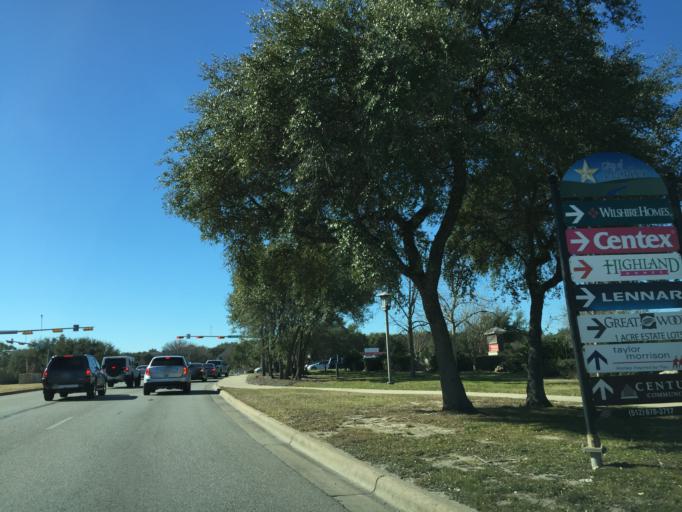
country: US
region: Texas
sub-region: Williamson County
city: Leander
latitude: 30.5525
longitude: -97.8551
